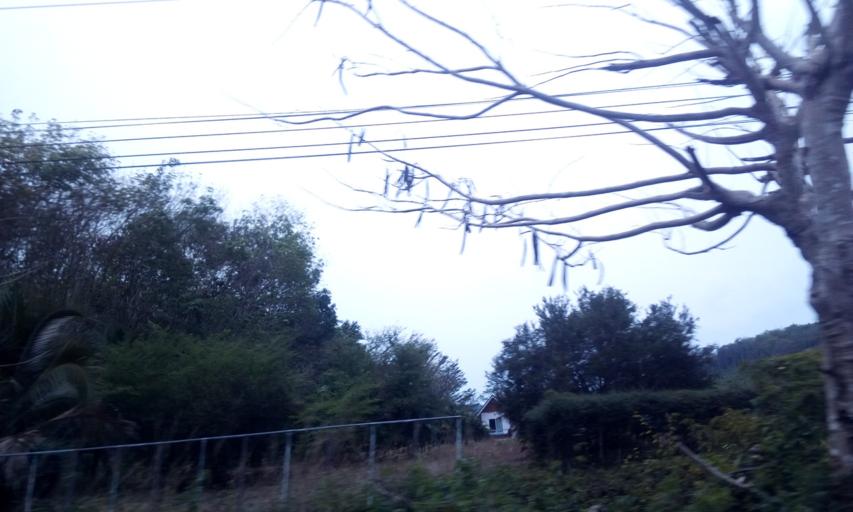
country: TH
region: Trat
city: Laem Ngop
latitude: 12.2750
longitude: 102.3056
